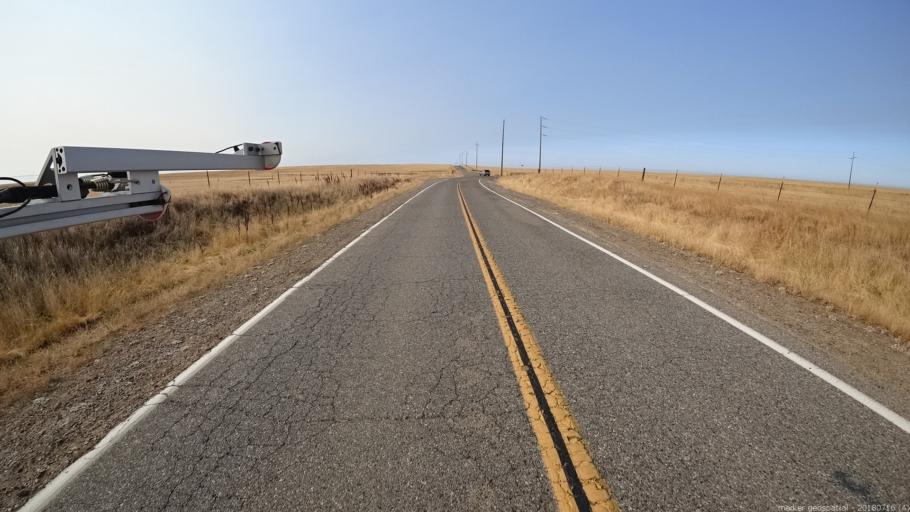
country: US
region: California
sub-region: Madera County
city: Madera Acres
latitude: 37.1275
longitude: -120.0203
